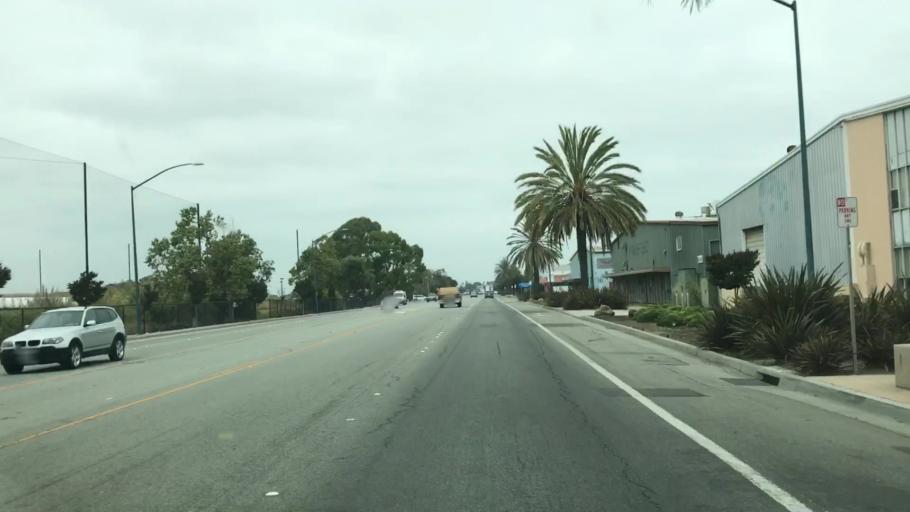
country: US
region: California
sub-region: Alameda County
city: San Leandro
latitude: 37.7189
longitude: -122.1902
